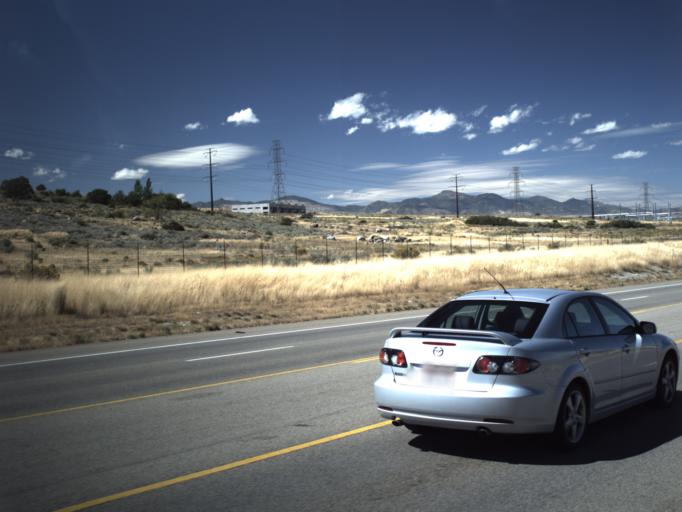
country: US
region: Utah
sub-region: Salt Lake County
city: Bluffdale
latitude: 40.4587
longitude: -111.9409
